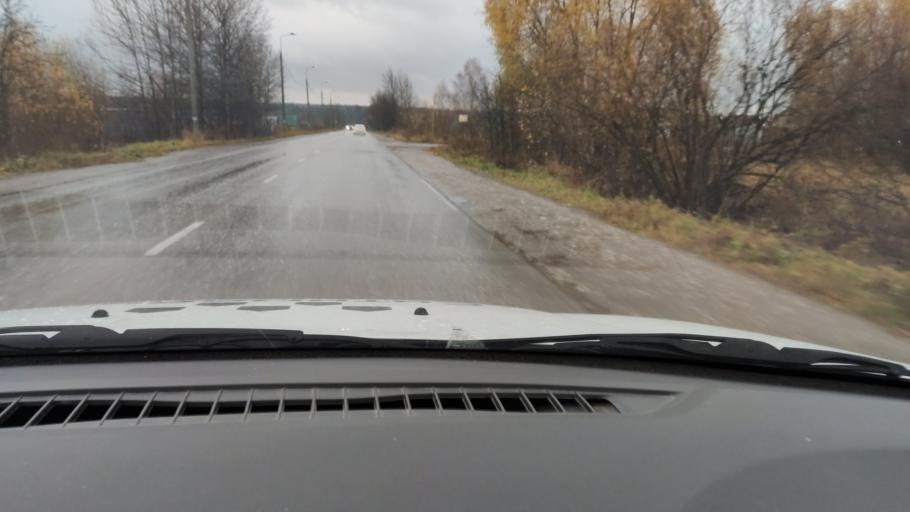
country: RU
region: Perm
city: Novyye Lyady
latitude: 58.0456
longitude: 56.5924
